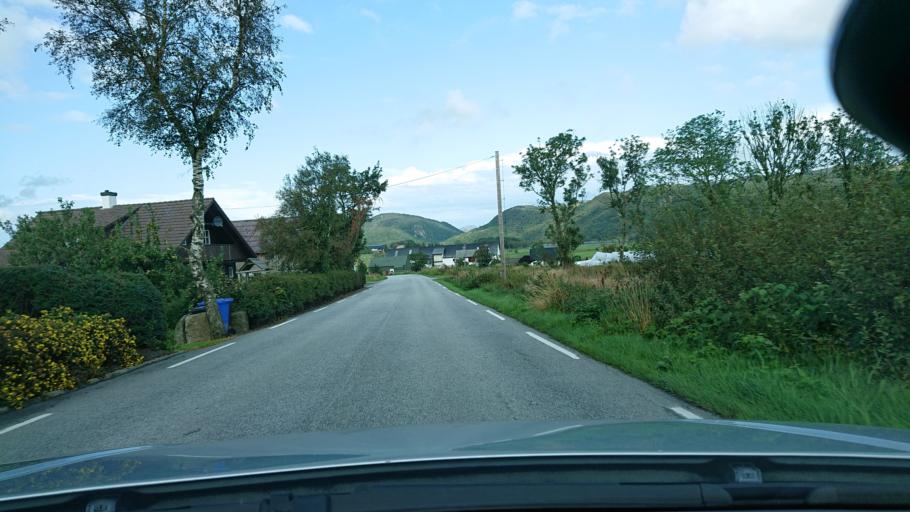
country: NO
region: Rogaland
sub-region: Gjesdal
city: Algard
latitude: 58.6956
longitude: 5.7790
